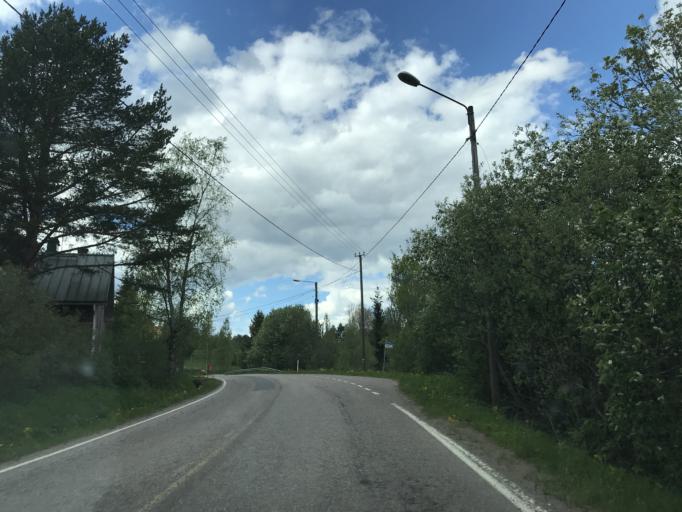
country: FI
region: Uusimaa
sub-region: Helsinki
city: Nurmijaervi
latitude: 60.4298
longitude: 24.7115
